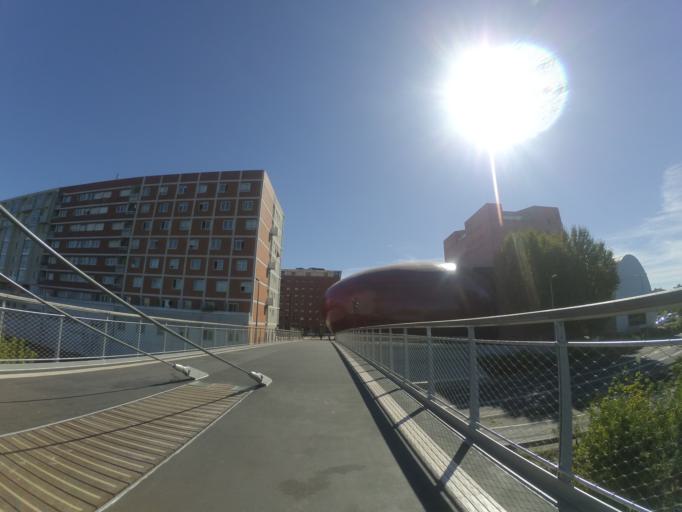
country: FR
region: Languedoc-Roussillon
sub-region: Departement des Pyrenees-Orientales
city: Perpignan
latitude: 42.7023
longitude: 2.8886
